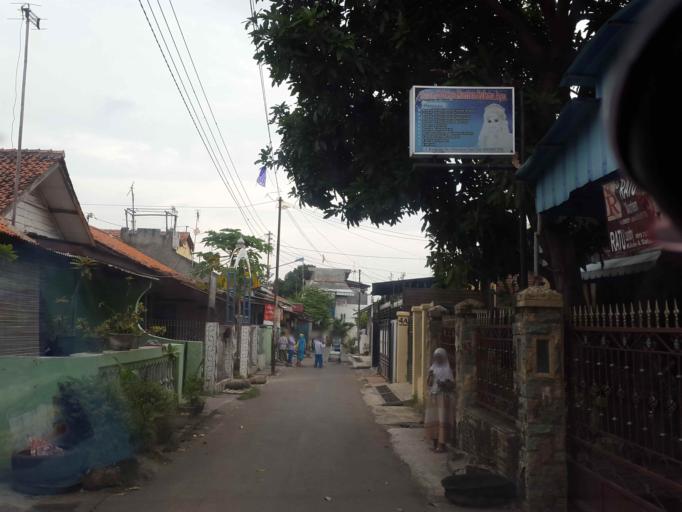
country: ID
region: Central Java
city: Tegal
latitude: -6.8722
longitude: 109.1312
